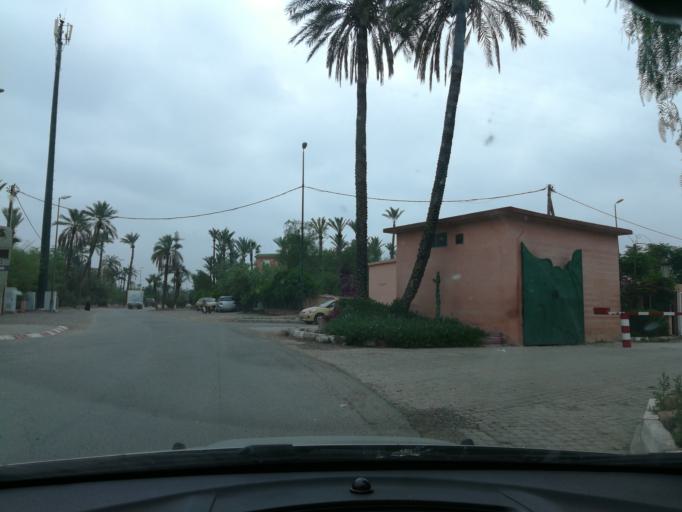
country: MA
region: Marrakech-Tensift-Al Haouz
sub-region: Marrakech
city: Marrakesh
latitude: 31.6820
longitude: -7.9851
